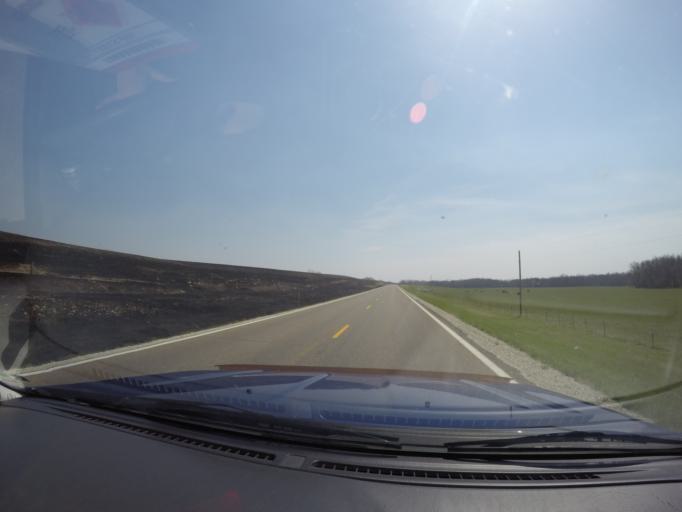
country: US
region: Kansas
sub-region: Chase County
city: Cottonwood Falls
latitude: 38.4771
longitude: -96.5568
